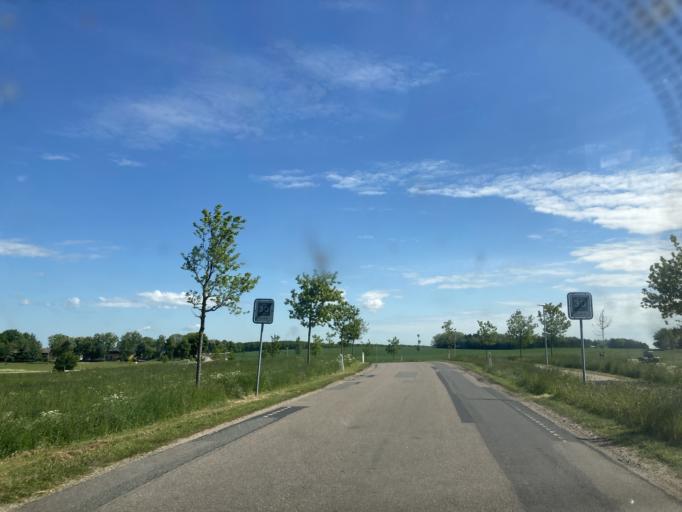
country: DK
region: Capital Region
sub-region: Hoje-Taastrup Kommune
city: Flong
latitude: 55.6291
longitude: 12.1910
